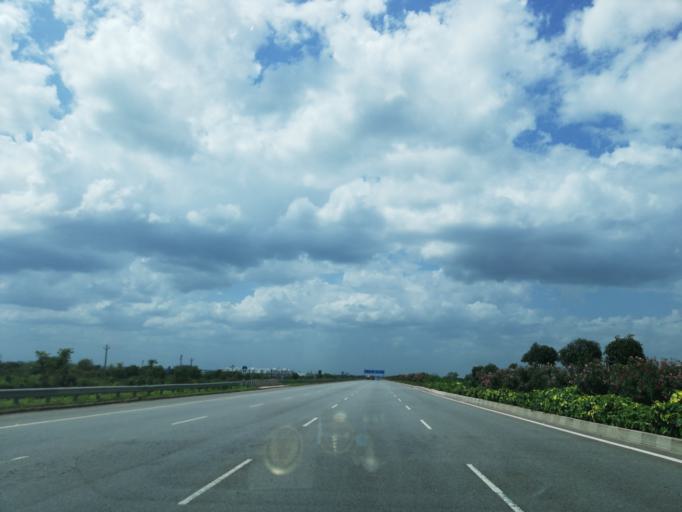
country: IN
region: Telangana
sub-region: Medak
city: Serilingampalle
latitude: 17.4383
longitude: 78.2599
